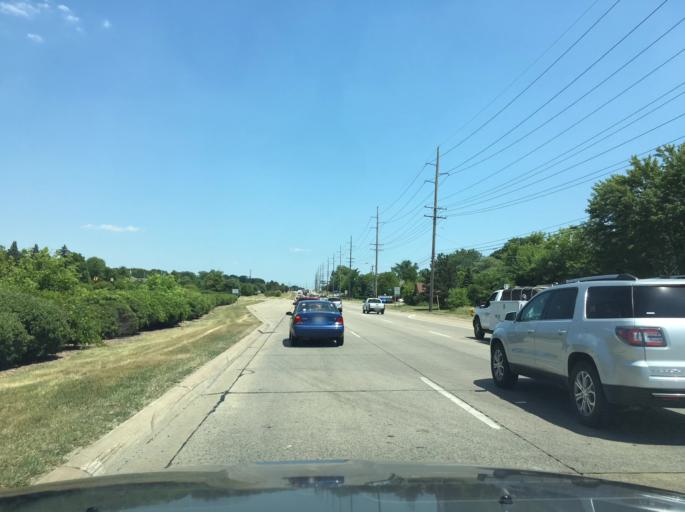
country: US
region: Michigan
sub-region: Macomb County
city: Mount Clemens
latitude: 42.6286
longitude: -82.8869
